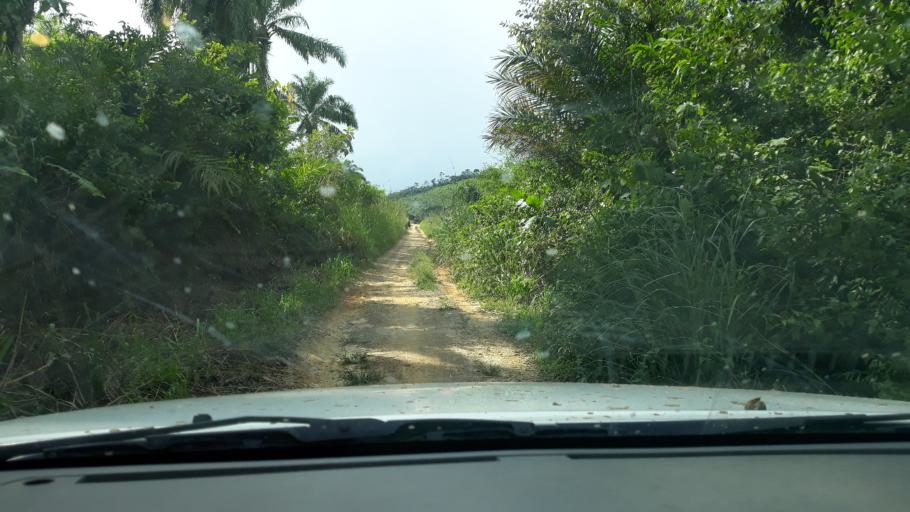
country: CD
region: Maniema
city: Kampene
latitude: -2.7531
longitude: 26.9248
